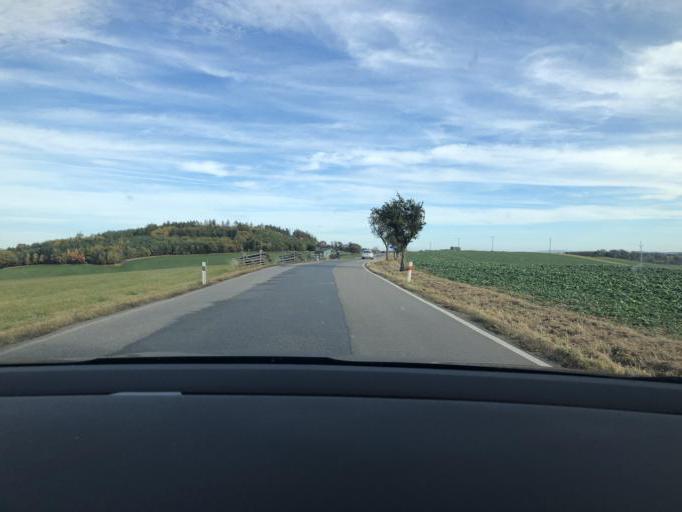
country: CZ
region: Central Bohemia
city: Divisov
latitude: 49.7873
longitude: 14.8353
